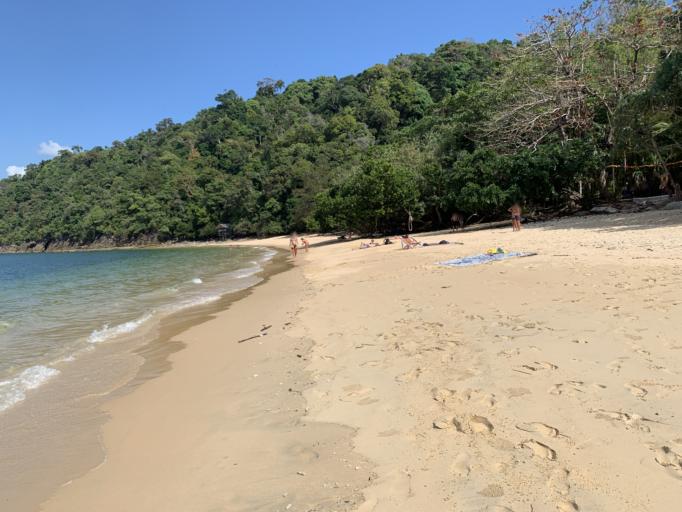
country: TH
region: Ranong
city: Kapoe
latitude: 9.7704
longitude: 98.4109
